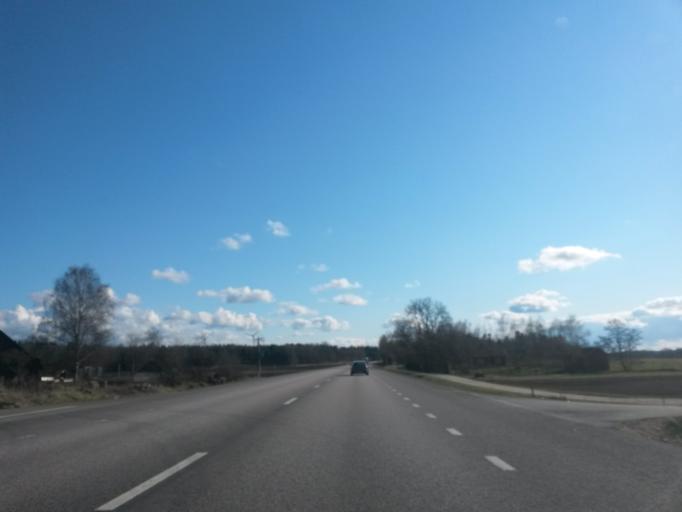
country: SE
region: Vaestra Goetaland
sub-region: Vargarda Kommun
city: Vargarda
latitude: 58.1344
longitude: 12.8598
